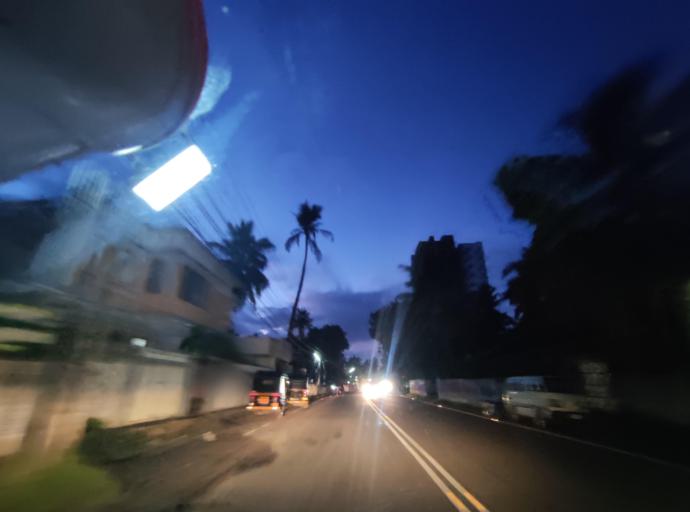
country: IN
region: Kerala
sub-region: Thiruvananthapuram
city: Thiruvananthapuram
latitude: 8.5464
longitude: 76.9599
